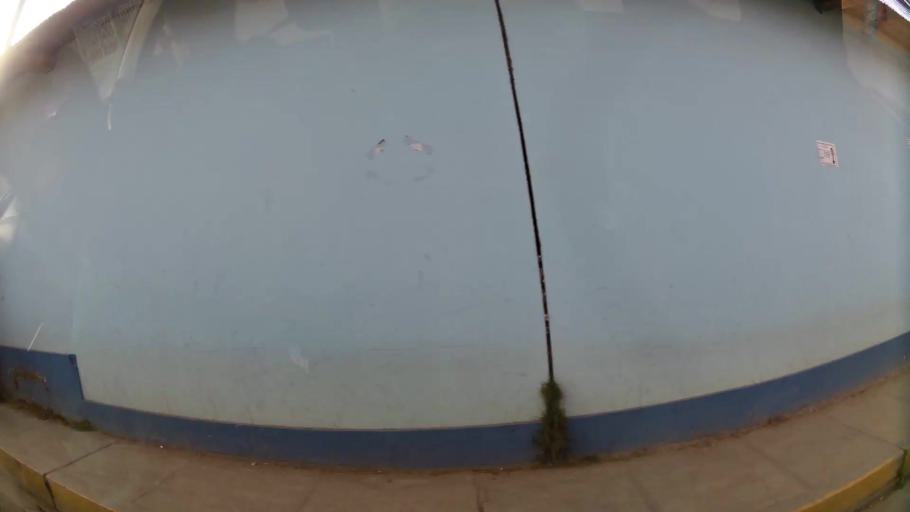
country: PE
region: Junin
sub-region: Provincia de Huancayo
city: Huancayo
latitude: -12.0474
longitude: -75.1994
